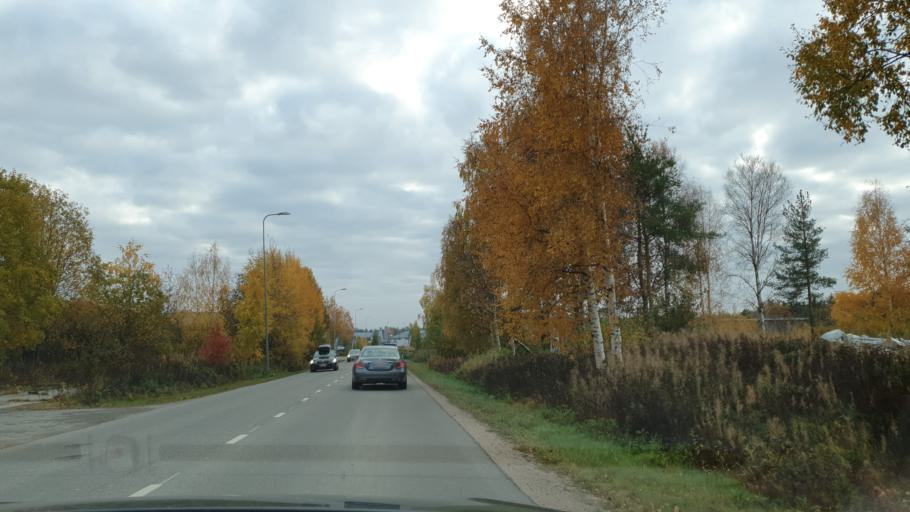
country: FI
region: Lapland
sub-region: Rovaniemi
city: Rovaniemi
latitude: 66.4935
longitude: 25.6775
